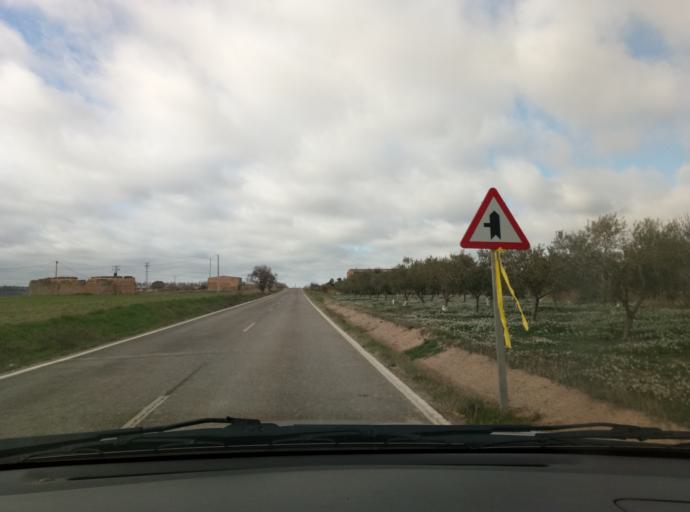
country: ES
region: Catalonia
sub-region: Provincia de Lleida
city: Vallbona de les Monges
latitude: 41.5620
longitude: 1.0667
